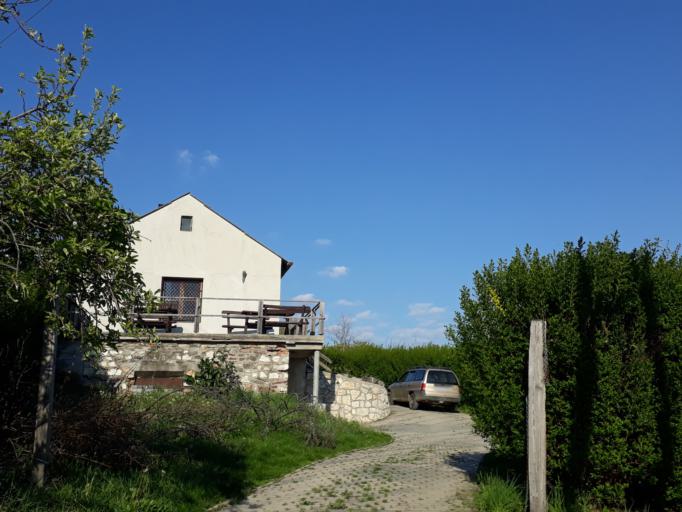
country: HU
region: Veszprem
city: Zanka
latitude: 46.9155
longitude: 17.6860
